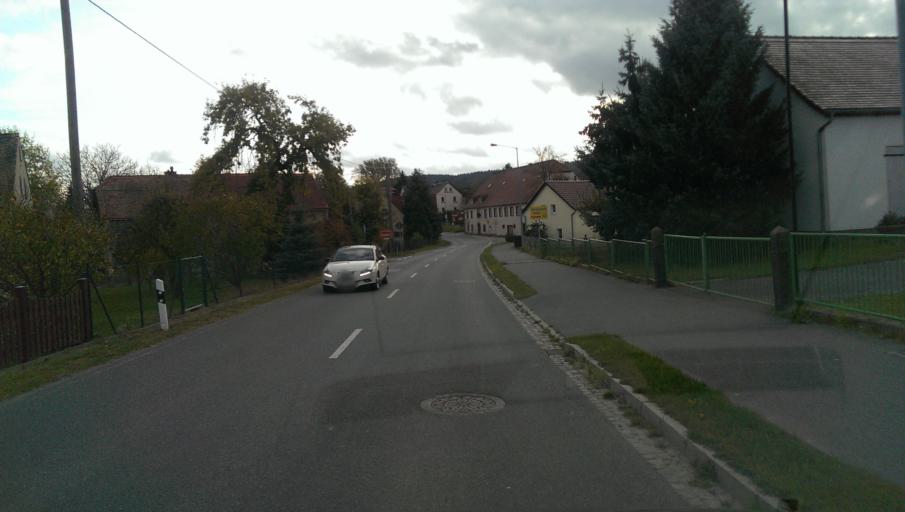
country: DE
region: Saxony
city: Elstra
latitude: 51.1995
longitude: 14.1349
